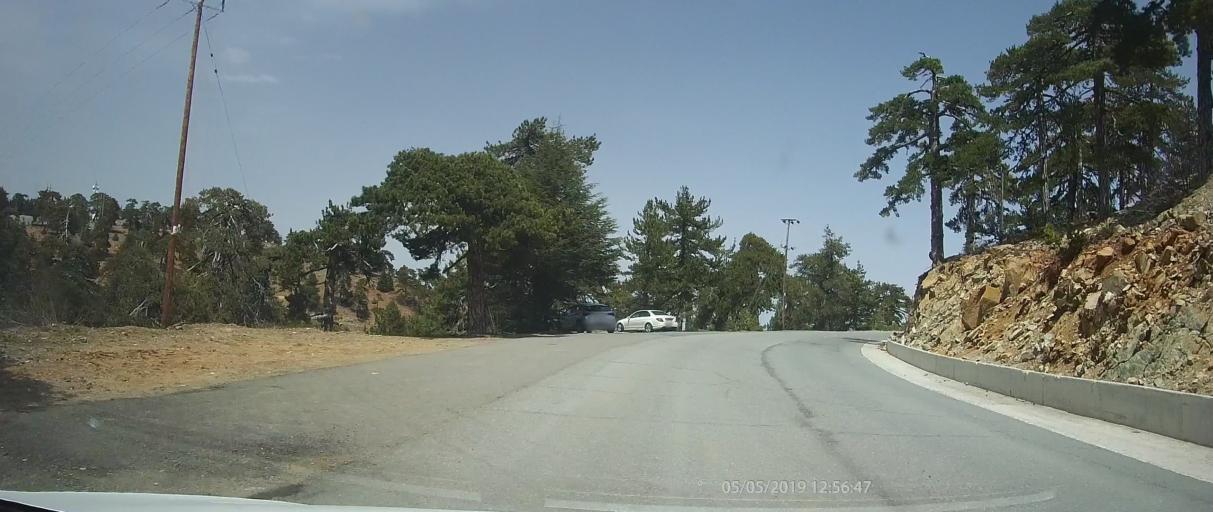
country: CY
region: Lefkosia
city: Kakopetria
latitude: 34.9398
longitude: 32.8656
